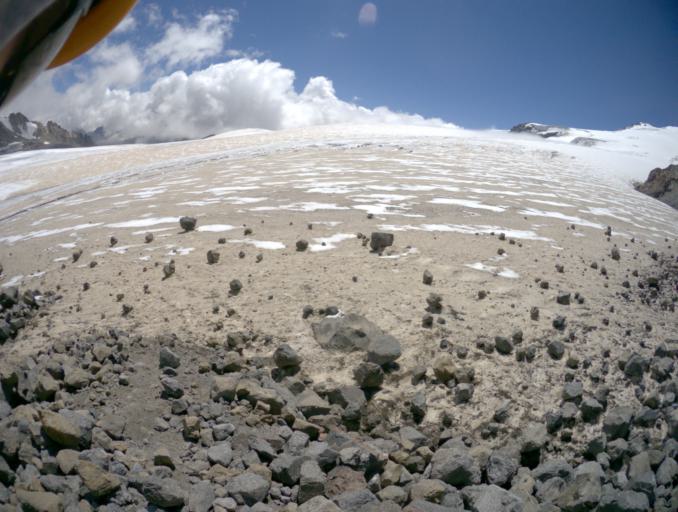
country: RU
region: Kabardino-Balkariya
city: Terskol
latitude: 43.3437
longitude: 42.5084
